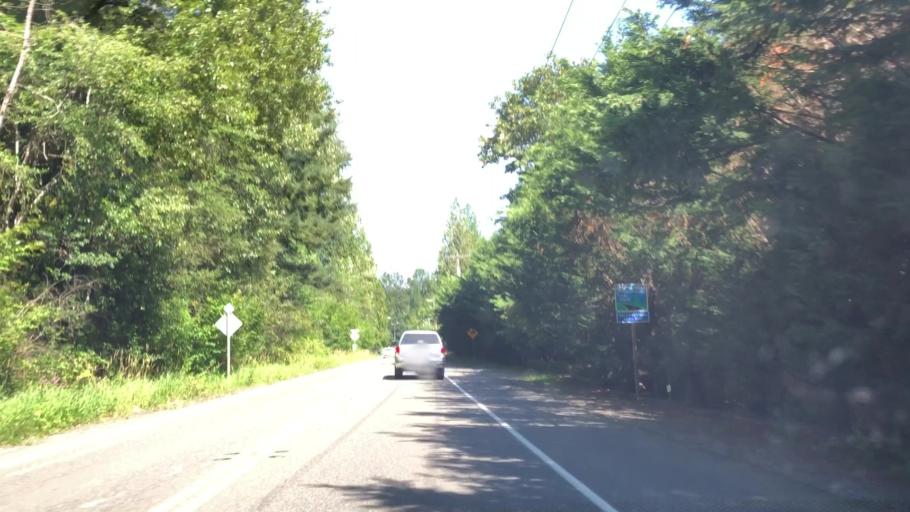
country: US
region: Washington
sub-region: King County
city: Cottage Lake
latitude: 47.7181
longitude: -122.0798
